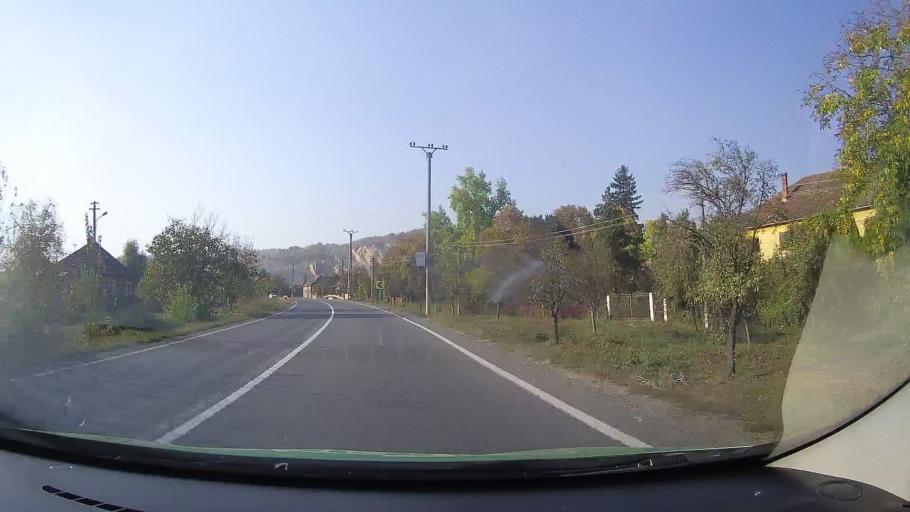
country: RO
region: Arad
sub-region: Comuna Zabrani
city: Neudorf
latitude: 46.1058
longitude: 21.6386
